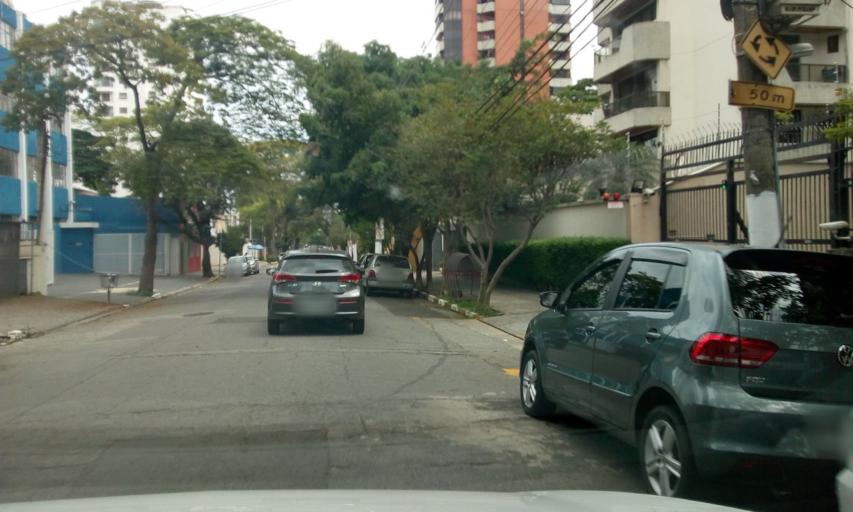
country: BR
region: Sao Paulo
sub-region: Sao Paulo
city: Sao Paulo
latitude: -23.6108
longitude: -46.6584
